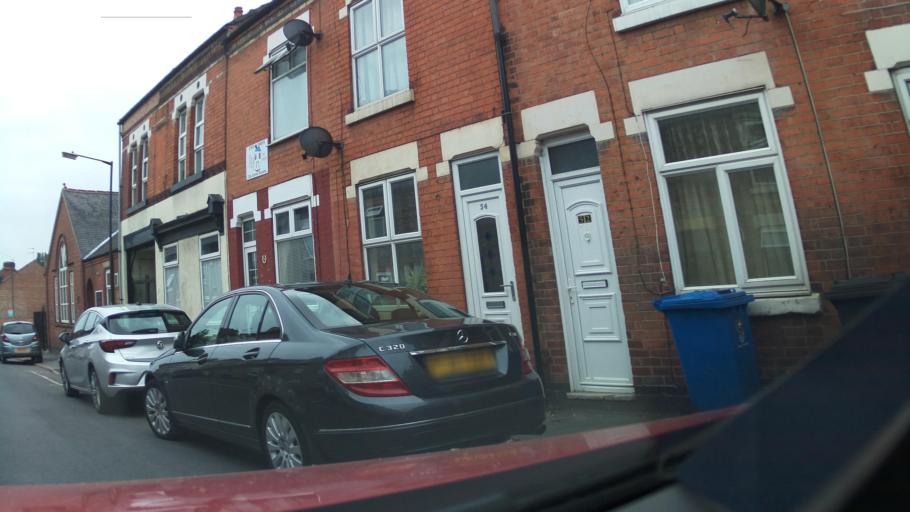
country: GB
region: England
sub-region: Derby
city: Derby
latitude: 52.9146
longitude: -1.4934
